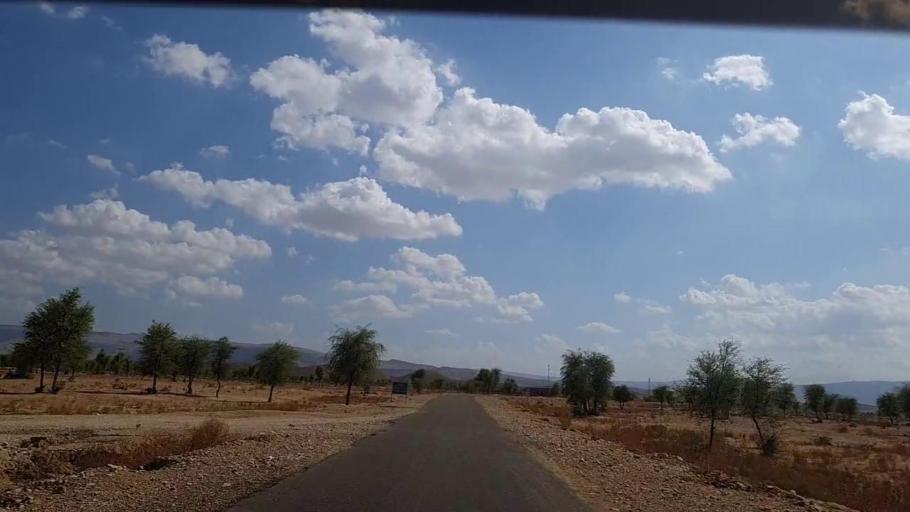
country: PK
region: Sindh
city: Johi
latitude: 26.5056
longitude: 67.4427
